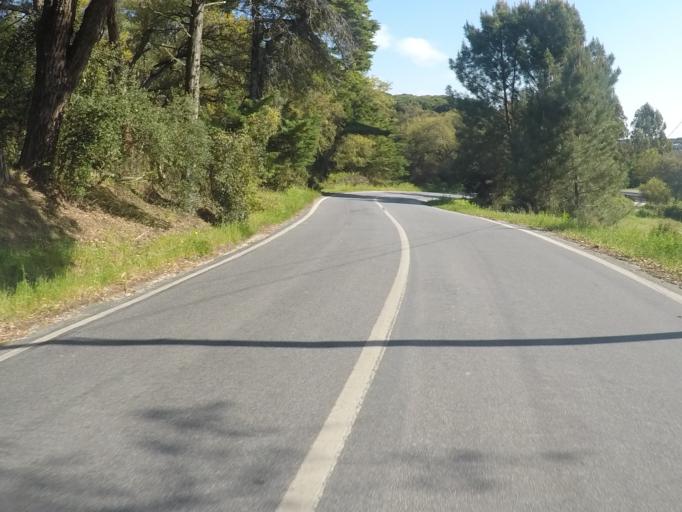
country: PT
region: Setubal
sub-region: Sesimbra
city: Sesimbra
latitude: 38.5001
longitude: -9.1513
